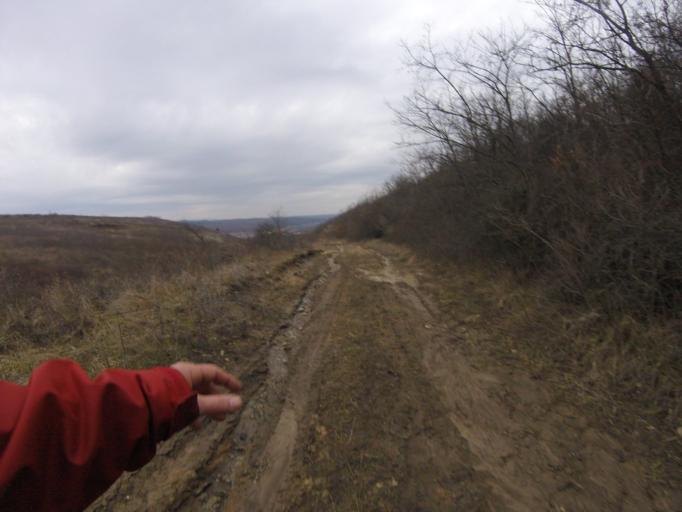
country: HU
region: Heves
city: Kerecsend
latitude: 47.8323
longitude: 20.3464
